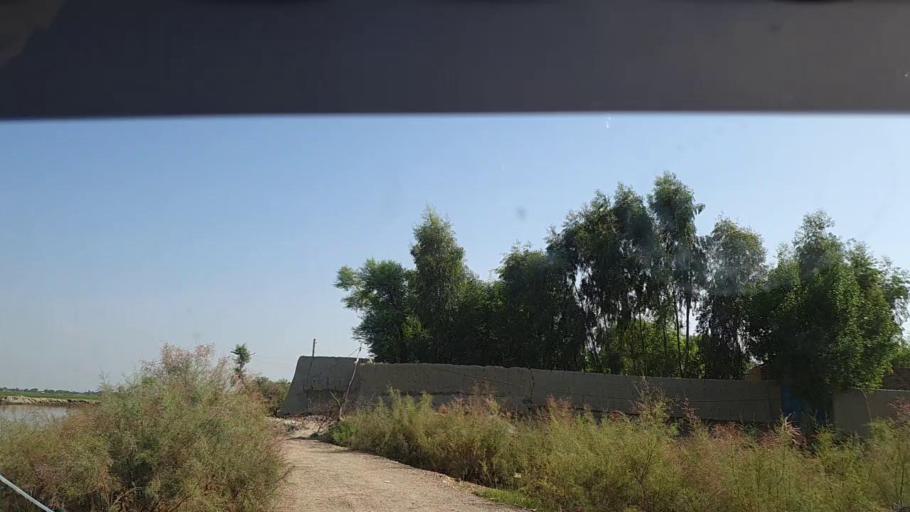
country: PK
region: Sindh
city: Ghauspur
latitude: 28.1791
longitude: 69.0284
